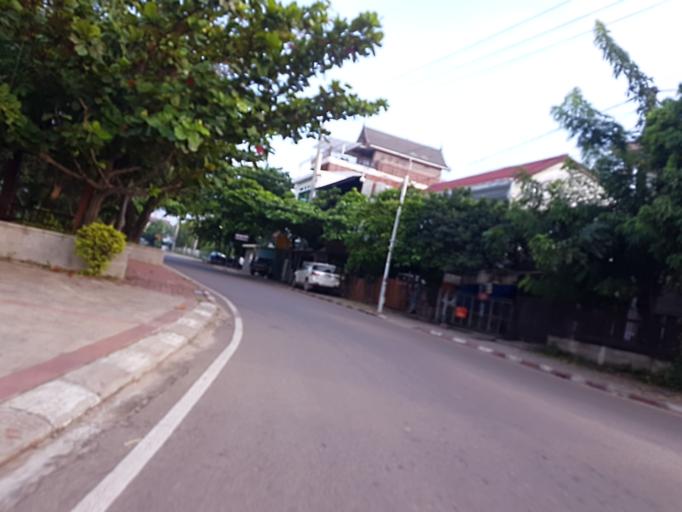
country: LA
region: Vientiane
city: Vientiane
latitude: 17.9533
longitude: 102.6173
